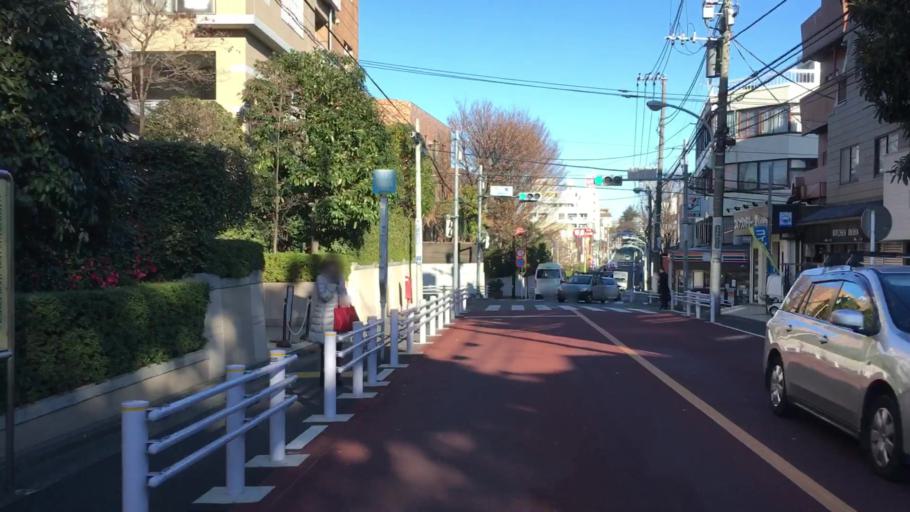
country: JP
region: Tokyo
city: Tokyo
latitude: 35.6202
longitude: 139.6672
